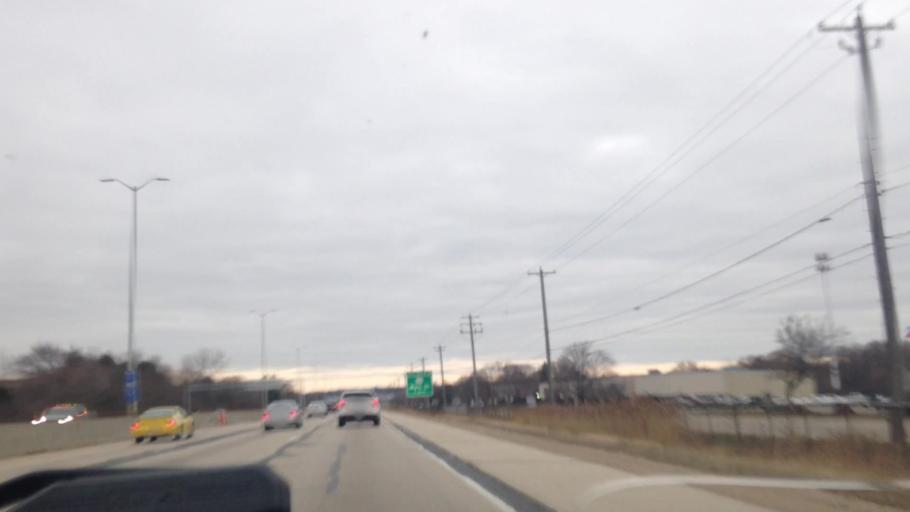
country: US
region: Wisconsin
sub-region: Waukesha County
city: Menomonee Falls
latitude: 43.1667
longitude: -88.0731
